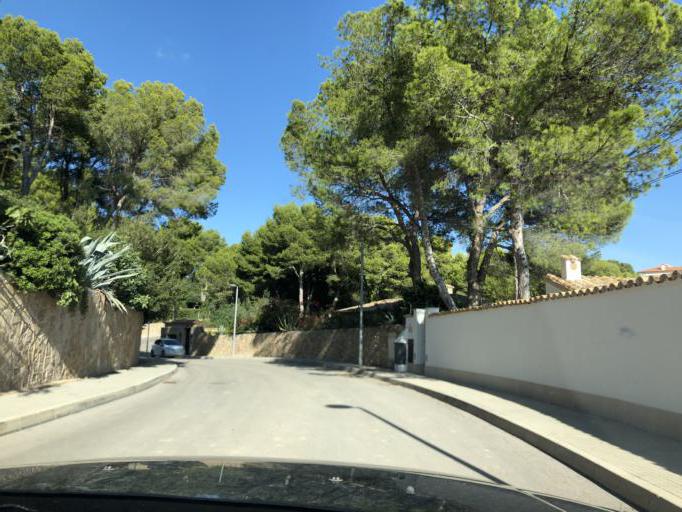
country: ES
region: Balearic Islands
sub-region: Illes Balears
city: Camp de Mar
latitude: 39.5395
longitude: 2.4133
